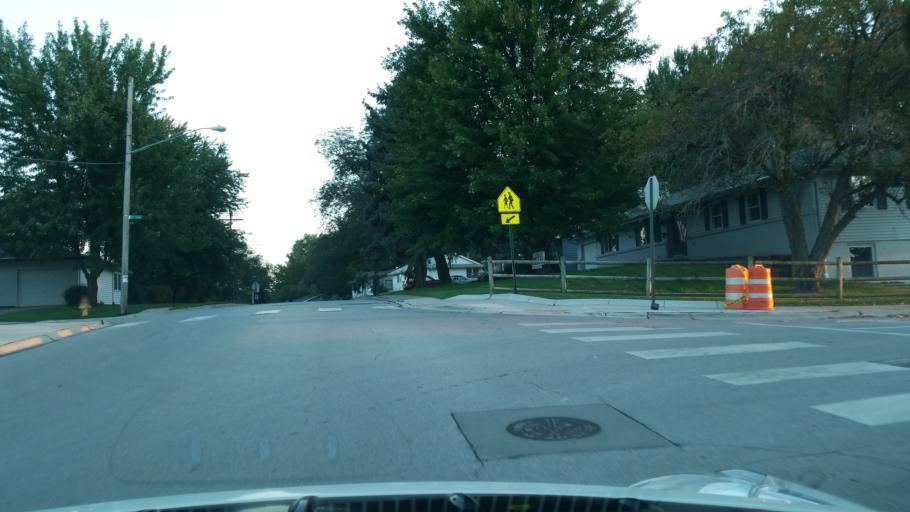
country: US
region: Nebraska
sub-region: Sarpy County
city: Bellevue
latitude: 41.1455
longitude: -95.9017
